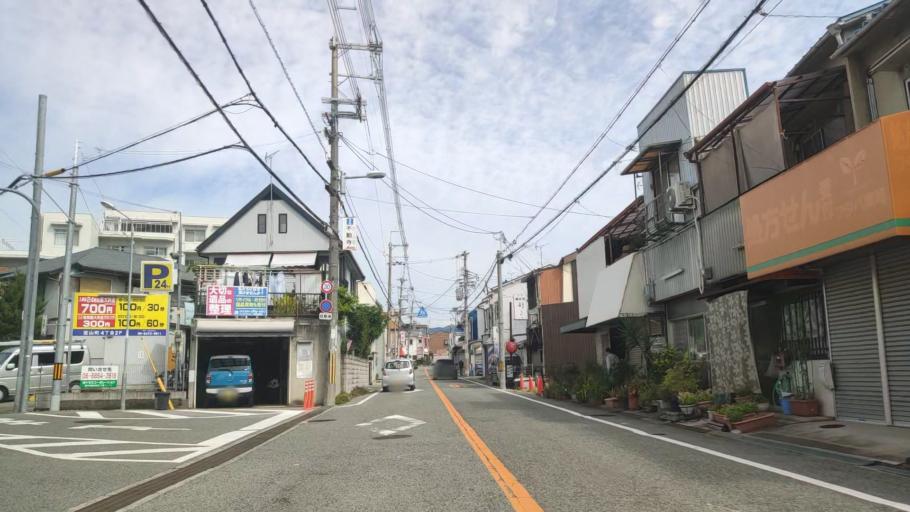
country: JP
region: Osaka
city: Mino
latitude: 34.8078
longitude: 135.4651
